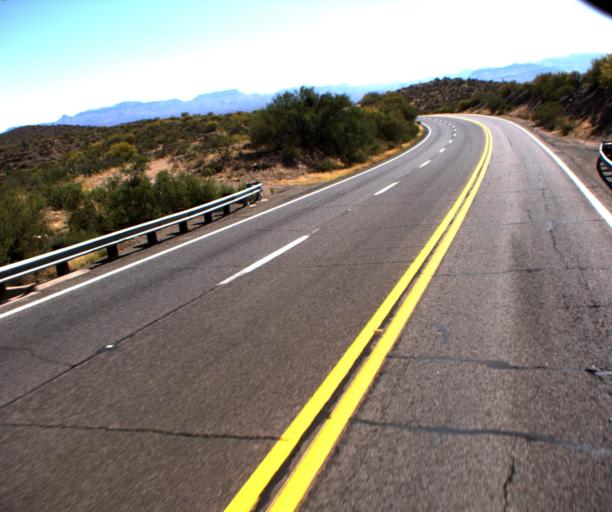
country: US
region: Arizona
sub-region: Pinal County
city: Mammoth
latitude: 32.6649
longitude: -110.6798
